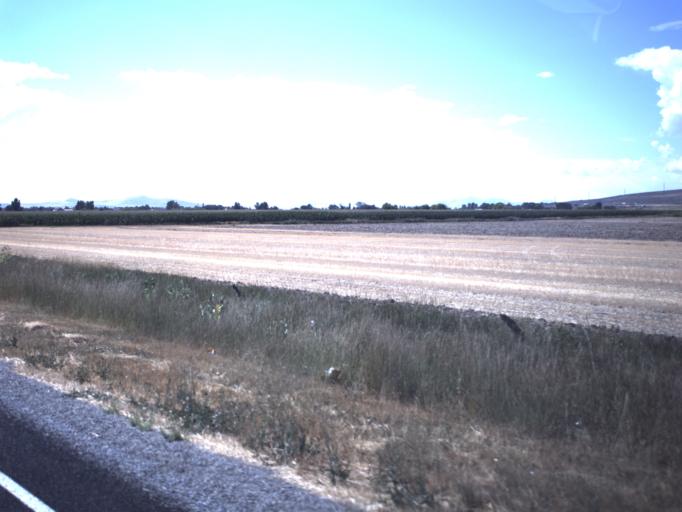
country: US
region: Utah
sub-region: Box Elder County
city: Garland
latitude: 41.7675
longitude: -112.1489
